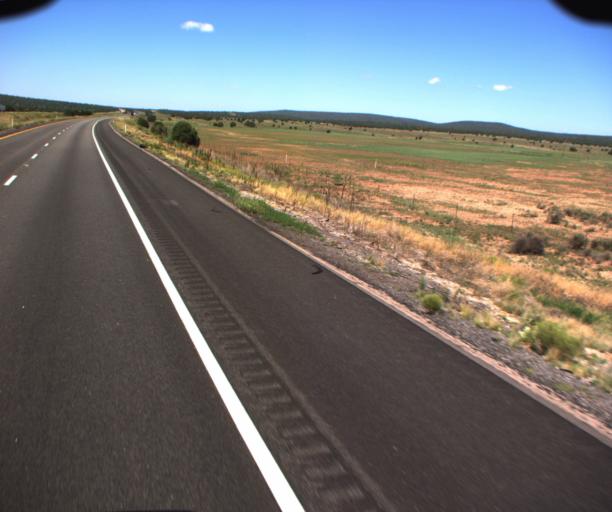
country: US
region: Arizona
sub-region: Mohave County
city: Peach Springs
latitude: 35.2349
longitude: -113.2115
